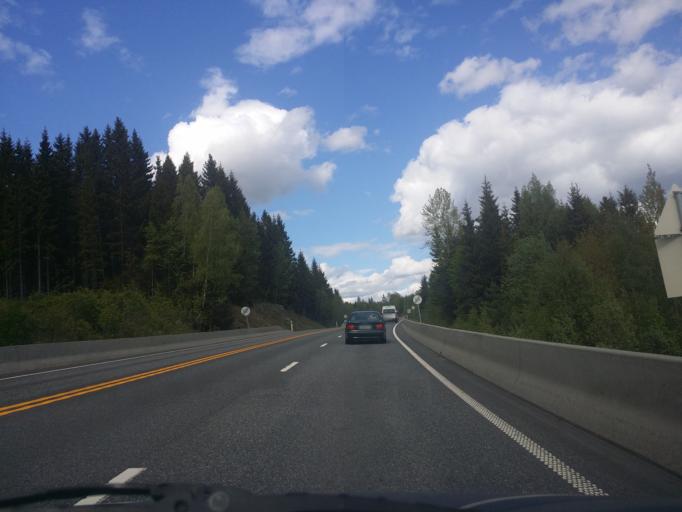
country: NO
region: Oppland
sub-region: Jevnaker
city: Jevnaker
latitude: 60.2679
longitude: 10.5008
